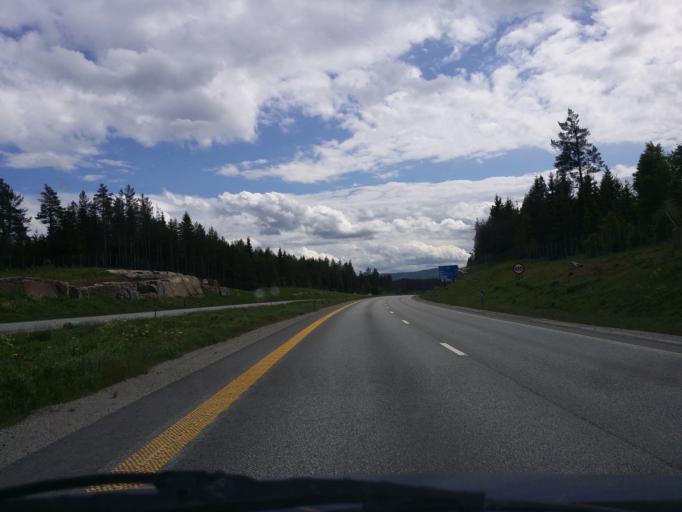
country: NO
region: Hedmark
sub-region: Stange
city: Stange
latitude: 60.6867
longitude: 11.2818
